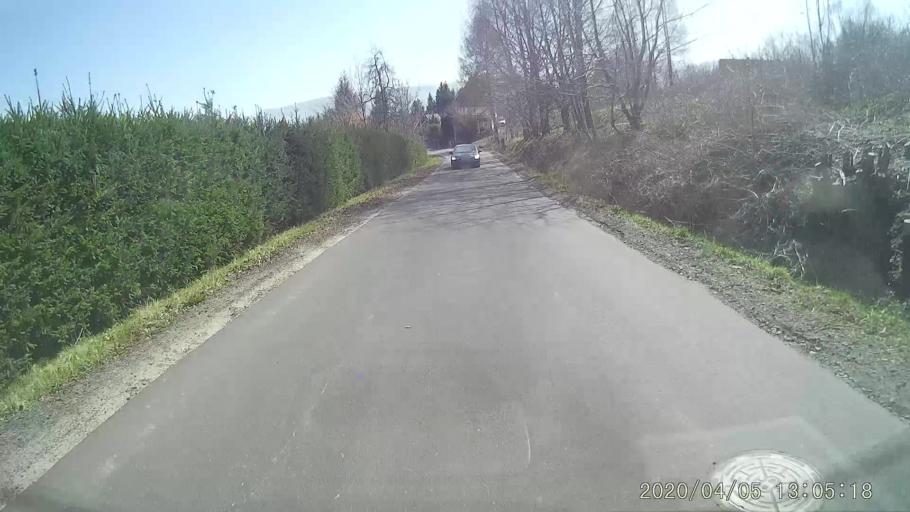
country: PL
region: Lower Silesian Voivodeship
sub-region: Powiat lwowecki
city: Mirsk
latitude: 50.9850
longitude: 15.3378
